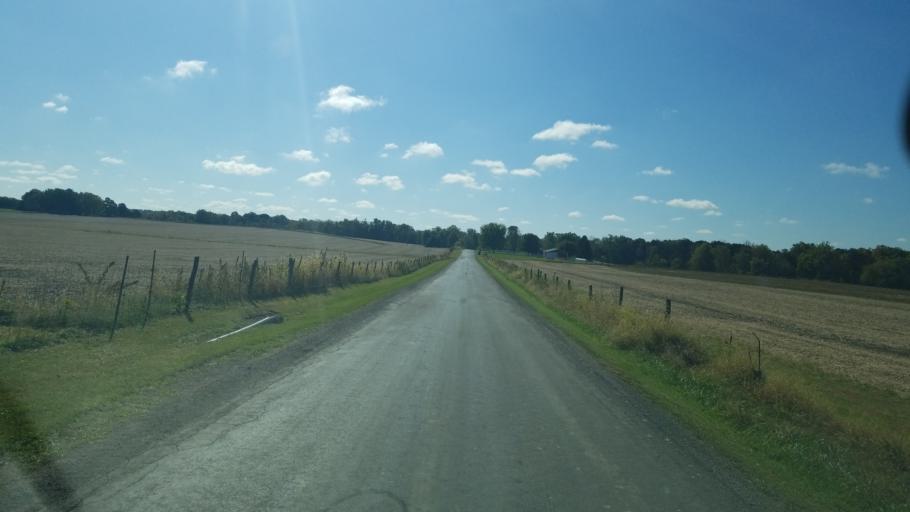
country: US
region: Ohio
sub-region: Highland County
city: Leesburg
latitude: 39.2703
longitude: -83.5527
